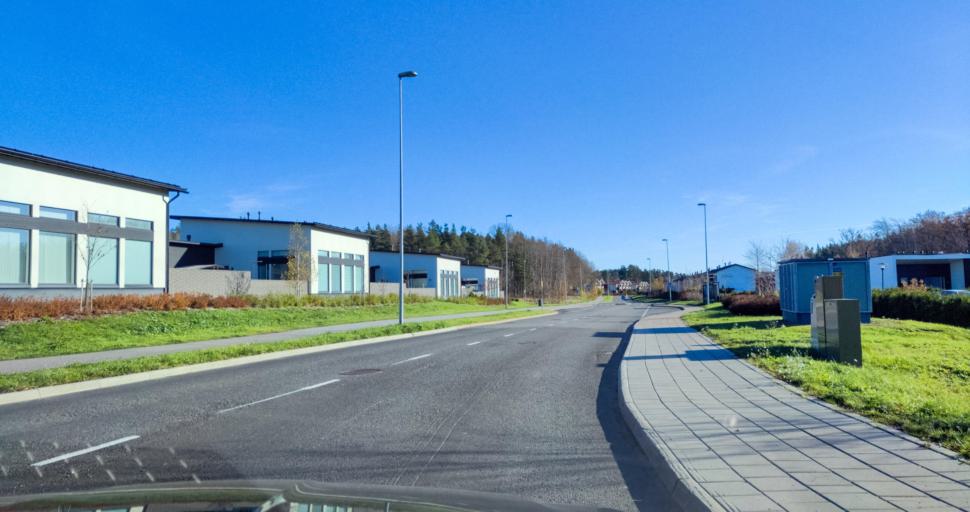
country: FI
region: Varsinais-Suomi
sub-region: Turku
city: Turku
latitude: 60.4115
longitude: 22.2084
